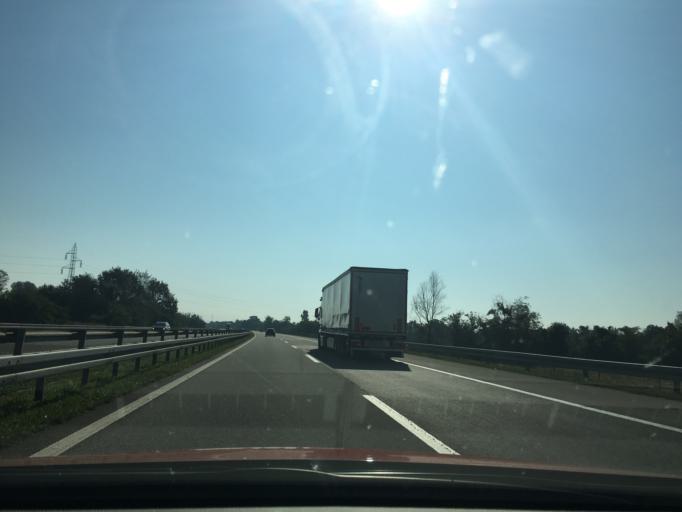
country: RS
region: Central Serbia
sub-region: Pomoravski Okrug
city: Jagodina
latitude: 43.9724
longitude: 21.2961
